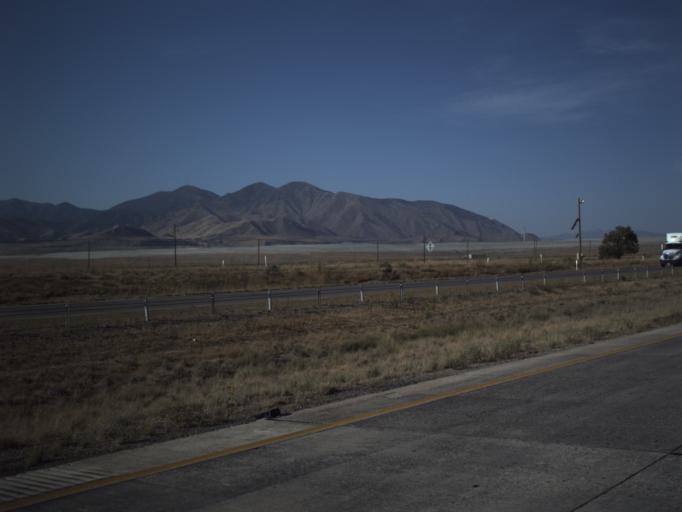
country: US
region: Utah
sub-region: Salt Lake County
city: Magna
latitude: 40.7711
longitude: -112.0659
